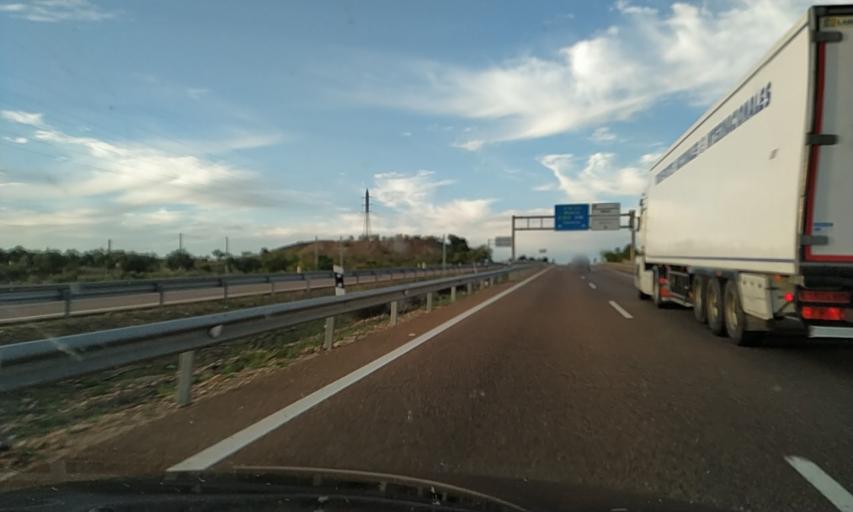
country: ES
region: Extremadura
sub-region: Provincia de Badajoz
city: Merida
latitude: 38.9322
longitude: -6.3667
